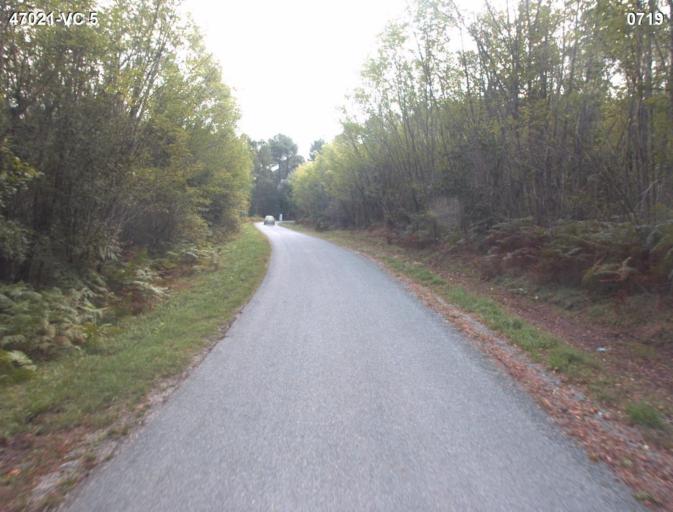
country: FR
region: Aquitaine
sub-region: Departement du Lot-et-Garonne
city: Barbaste
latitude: 44.1421
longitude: 0.2870
